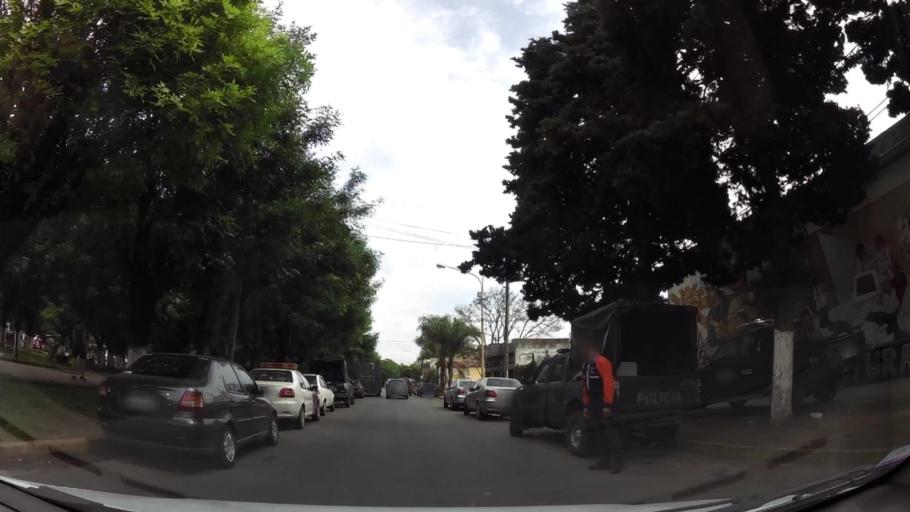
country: AR
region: Buenos Aires F.D.
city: Villa Lugano
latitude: -34.6990
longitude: -58.5069
